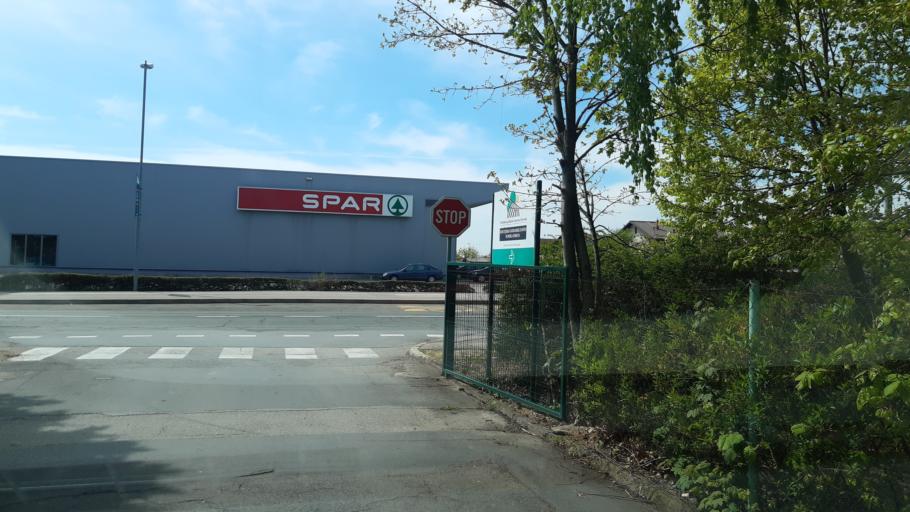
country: SI
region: Murska Sobota
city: Cernelavci
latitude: 46.6629
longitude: 16.1455
